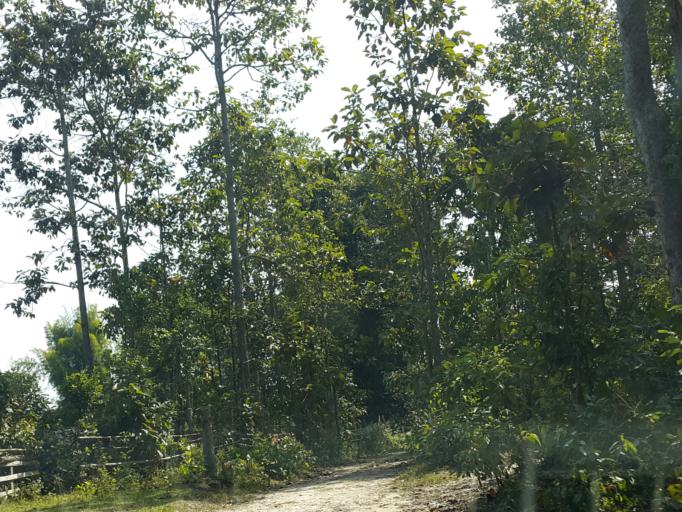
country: TH
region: Chiang Mai
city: Hot
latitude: 18.1214
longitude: 98.4413
